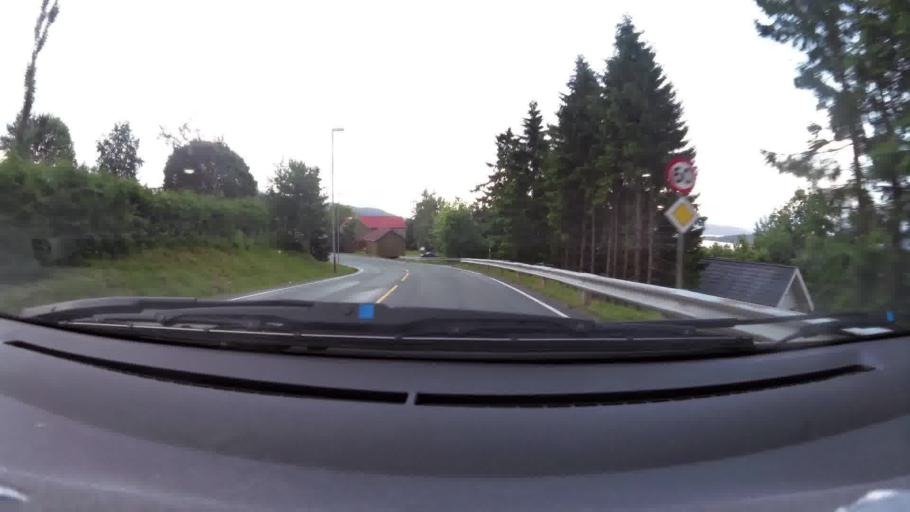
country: NO
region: More og Romsdal
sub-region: Molde
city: Molde
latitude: 62.7521
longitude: 7.2538
